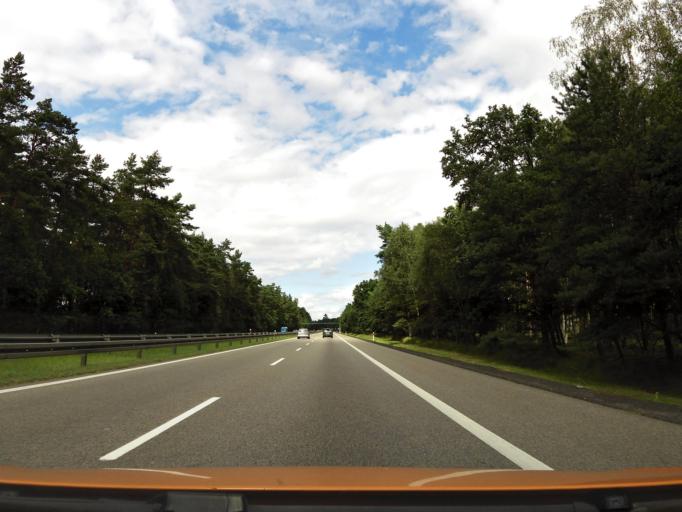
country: PL
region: West Pomeranian Voivodeship
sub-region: Powiat goleniowski
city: Goleniow
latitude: 53.4485
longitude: 14.7843
